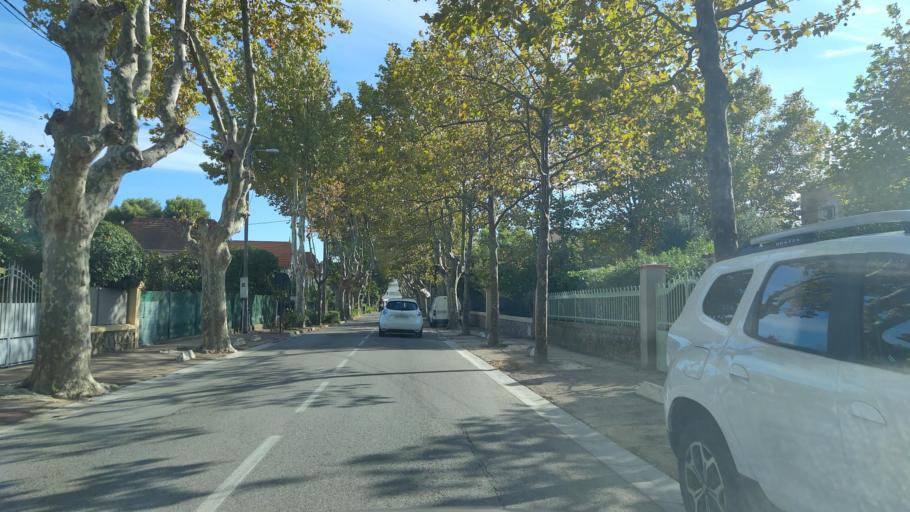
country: FR
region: Provence-Alpes-Cote d'Azur
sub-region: Departement du Var
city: La Seyne-sur-Mer
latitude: 43.0792
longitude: 5.8860
